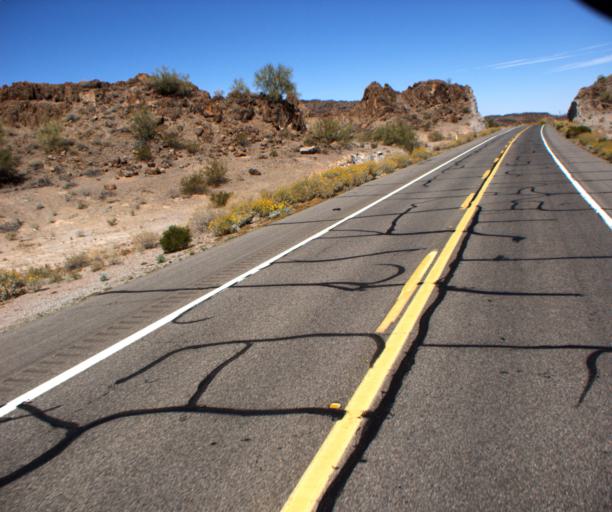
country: US
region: Arizona
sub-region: Pima County
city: Ajo
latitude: 32.5486
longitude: -112.8800
